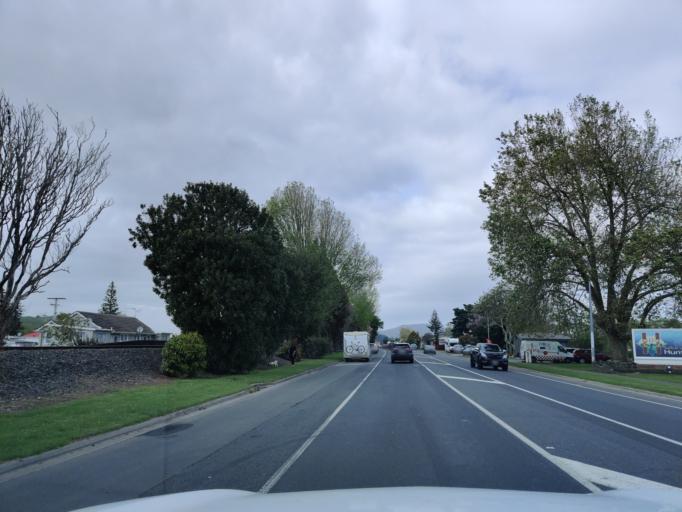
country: NZ
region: Waikato
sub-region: Waikato District
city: Ngaruawahia
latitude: -37.5484
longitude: 175.1585
